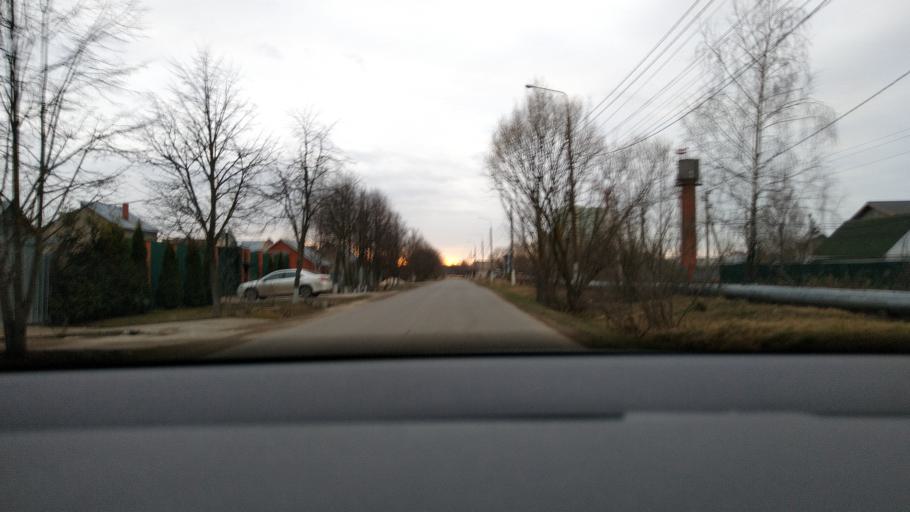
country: RU
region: Moscow
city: Vnukovo
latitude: 55.5903
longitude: 37.2161
